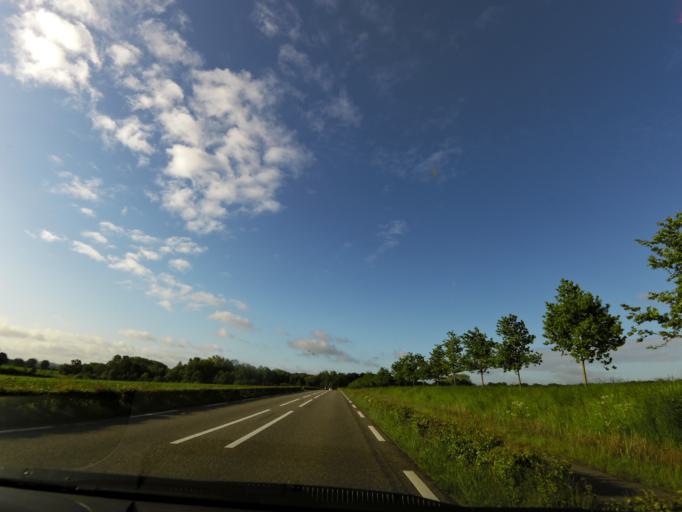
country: NL
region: Limburg
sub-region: Gemeente Voerendaal
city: Voerendaal
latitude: 50.8942
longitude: 5.9270
